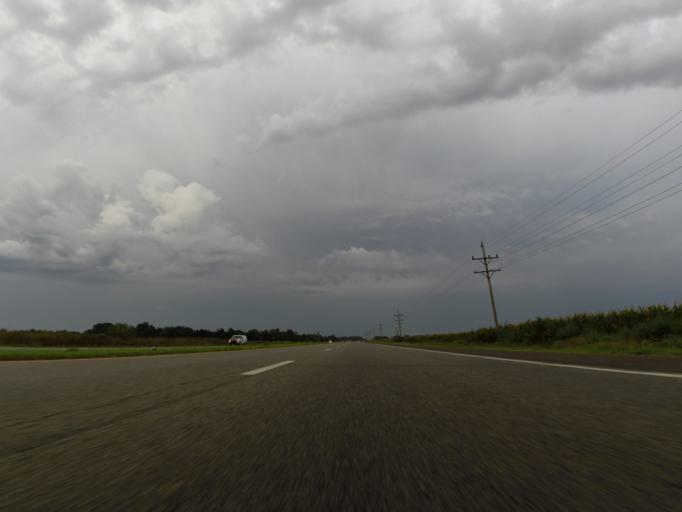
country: US
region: Kansas
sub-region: Reno County
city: South Hutchinson
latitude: 37.9969
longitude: -97.9406
